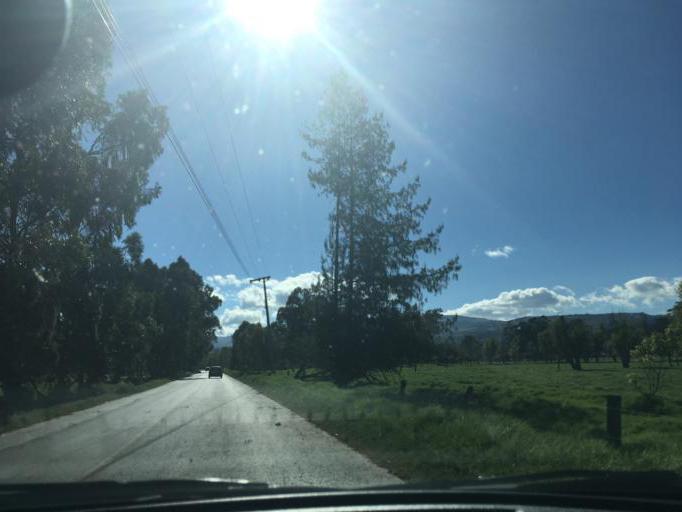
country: CO
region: Boyaca
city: Firavitoba
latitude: 5.6570
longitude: -72.9797
